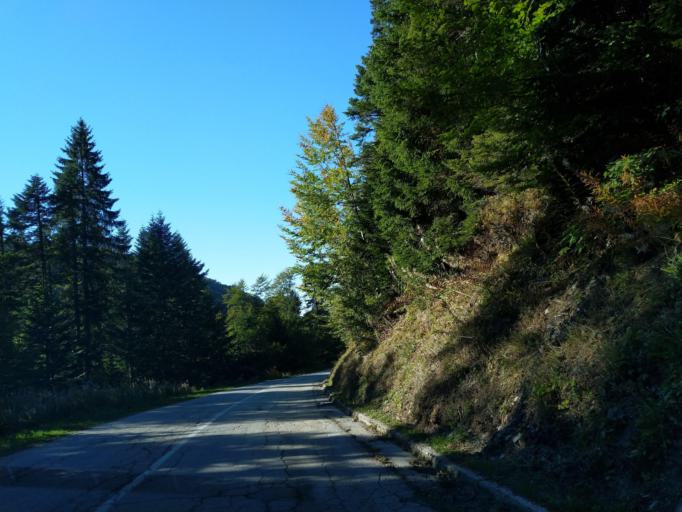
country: RS
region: Central Serbia
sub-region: Moravicki Okrug
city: Ivanjica
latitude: 43.4289
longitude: 20.2657
